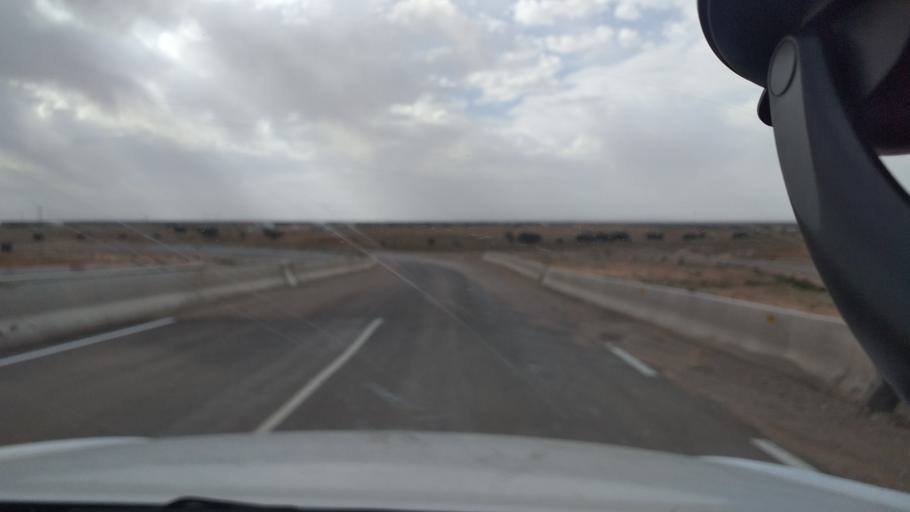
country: TN
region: Madanin
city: Medenine
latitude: 33.2991
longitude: 10.6087
